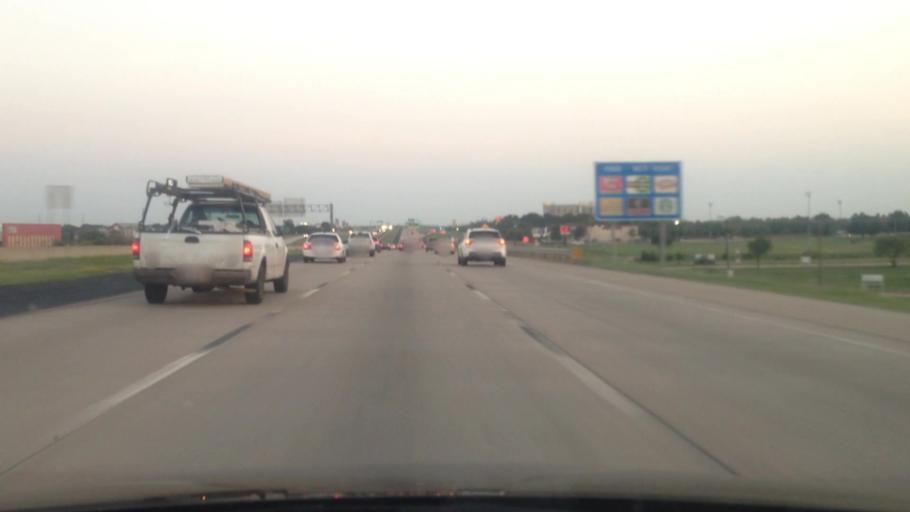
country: US
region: Texas
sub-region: Tarrant County
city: Grapevine
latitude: 32.8921
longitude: -97.0993
